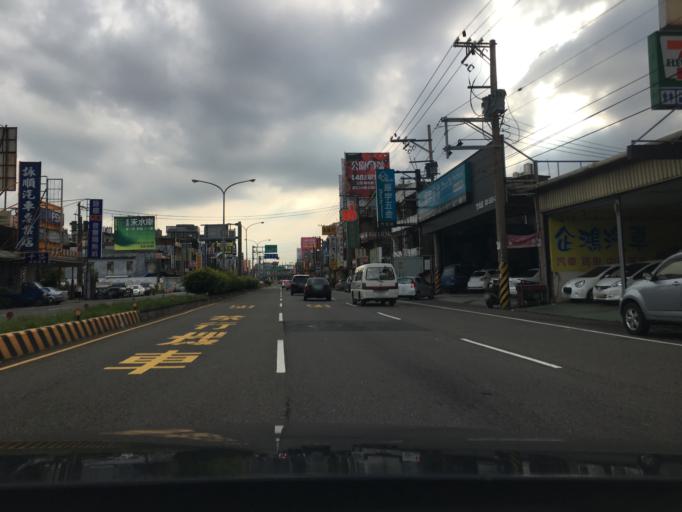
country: TW
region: Taiwan
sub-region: Hsinchu
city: Zhubei
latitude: 24.8307
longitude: 121.0017
